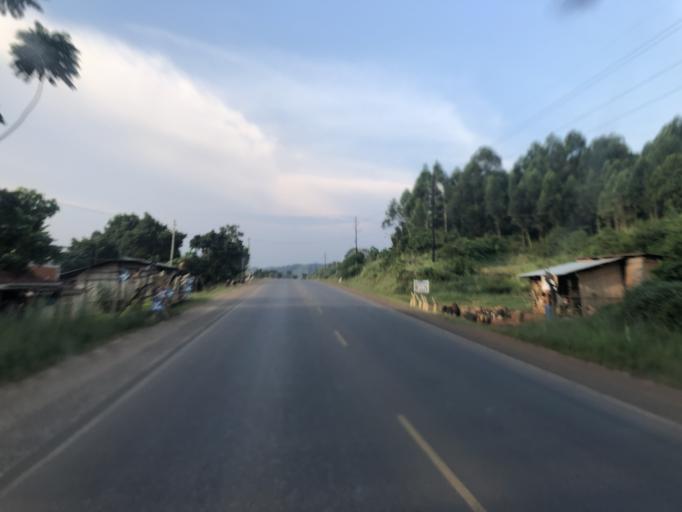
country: UG
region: Central Region
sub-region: Mpigi District
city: Mpigi
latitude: 0.1963
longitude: 32.2976
